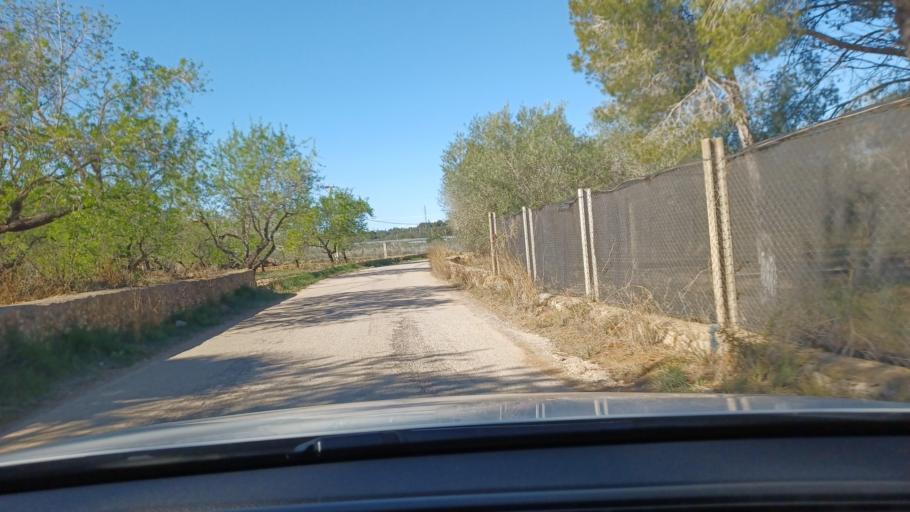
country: ES
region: Catalonia
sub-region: Provincia de Tarragona
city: Masdenverge
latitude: 40.6898
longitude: 0.5417
